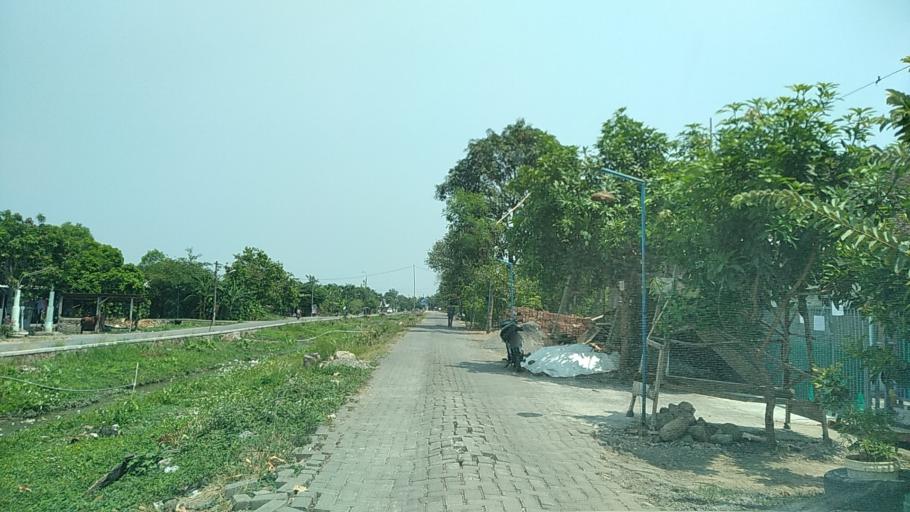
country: ID
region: Central Java
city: Mranggen
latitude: -7.0294
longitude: 110.4809
